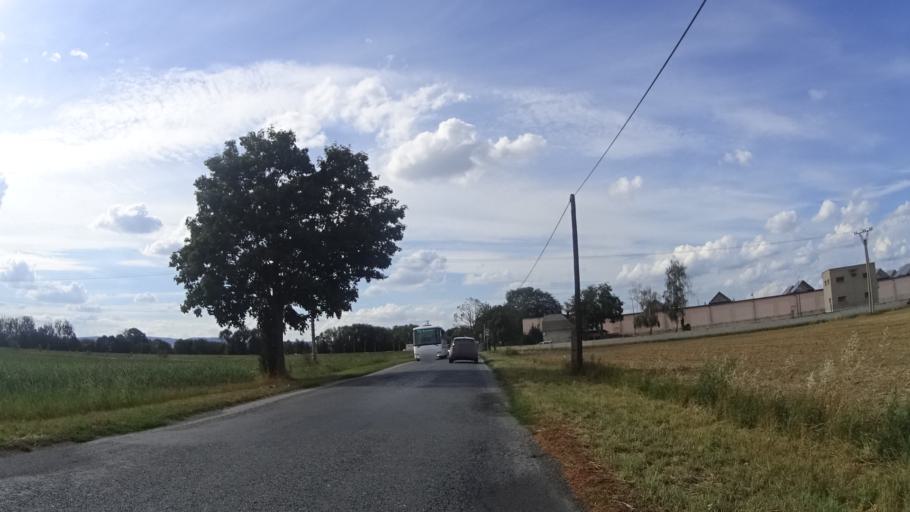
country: CZ
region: Olomoucky
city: Moravicany
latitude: 49.7518
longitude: 16.9676
